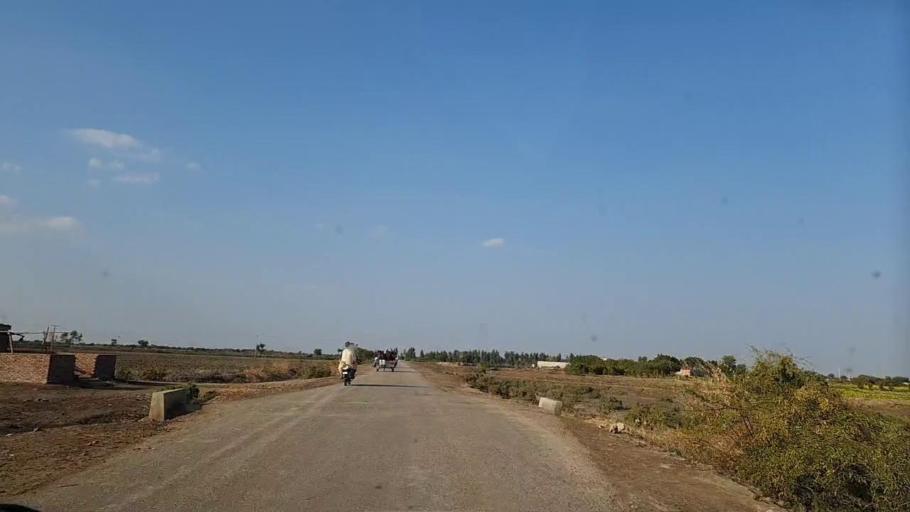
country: PK
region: Sindh
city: Pithoro
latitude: 25.7104
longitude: 69.2209
